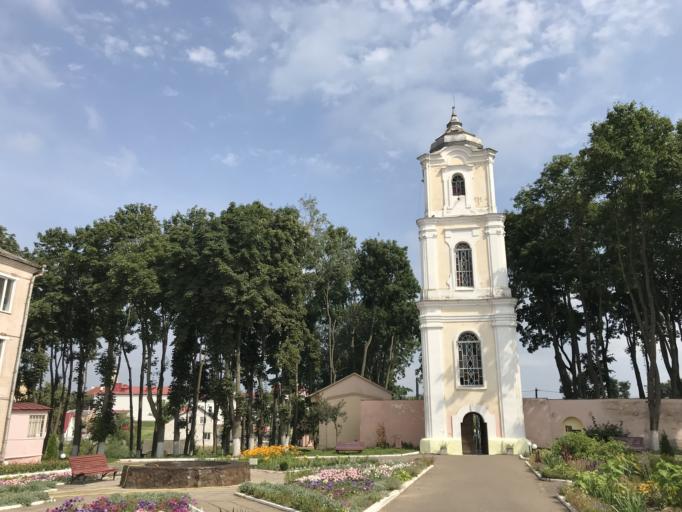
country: BY
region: Minsk
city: Nyasvizh
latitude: 53.2158
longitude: 26.6814
